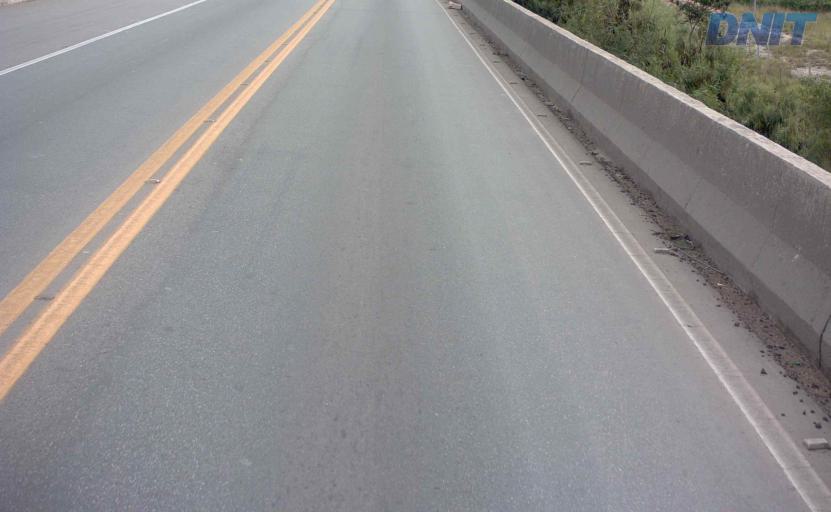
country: BR
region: Minas Gerais
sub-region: Santa Luzia
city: Santa Luzia
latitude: -19.8415
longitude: -43.8684
